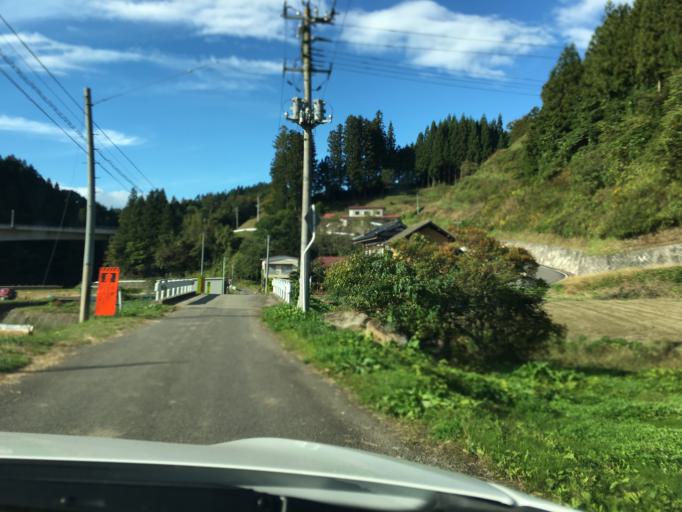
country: JP
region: Fukushima
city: Ishikawa
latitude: 37.1590
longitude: 140.5121
